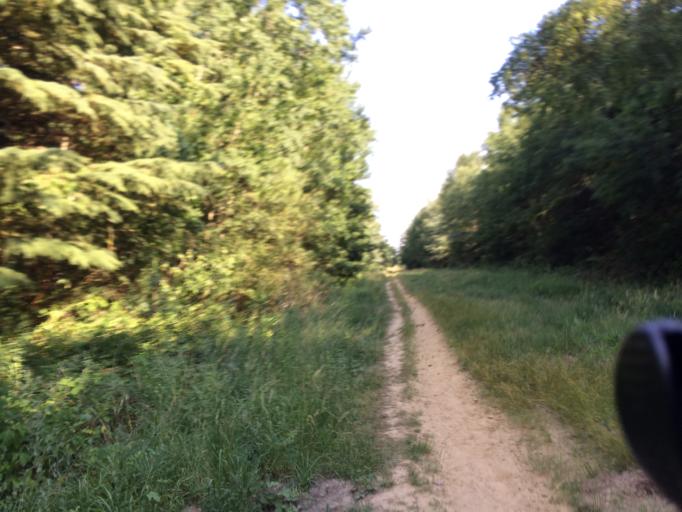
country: FR
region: Ile-de-France
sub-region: Departement de l'Essonne
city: Montgeron
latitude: 48.6795
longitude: 2.4479
